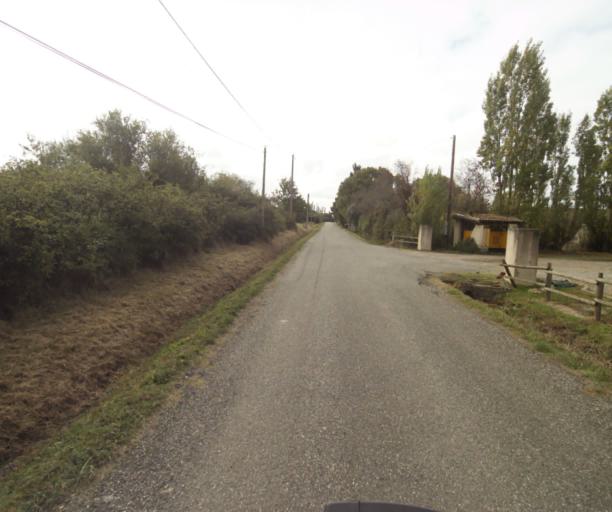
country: FR
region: Midi-Pyrenees
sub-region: Departement du Tarn-et-Garonne
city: Finhan
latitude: 43.9242
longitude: 1.2458
